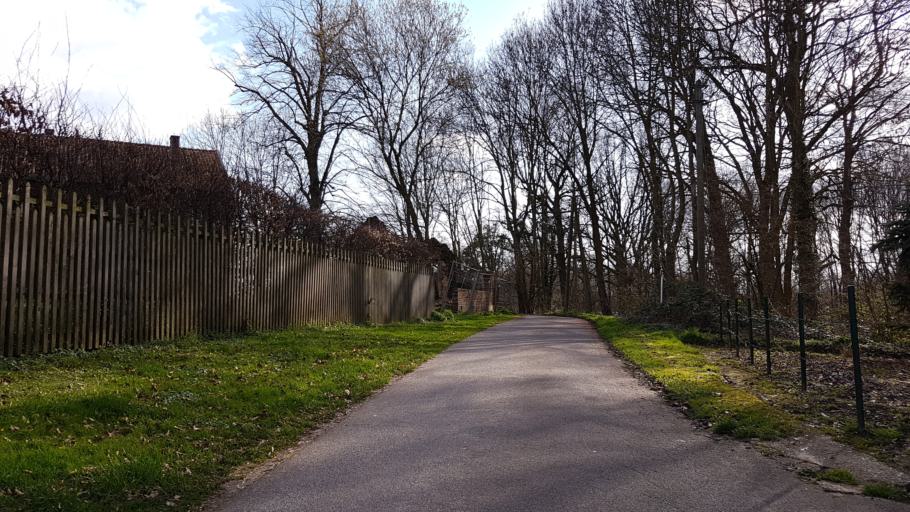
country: DE
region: North Rhine-Westphalia
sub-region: Regierungsbezirk Dusseldorf
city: Schwalmtal
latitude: 51.2273
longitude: 6.2532
